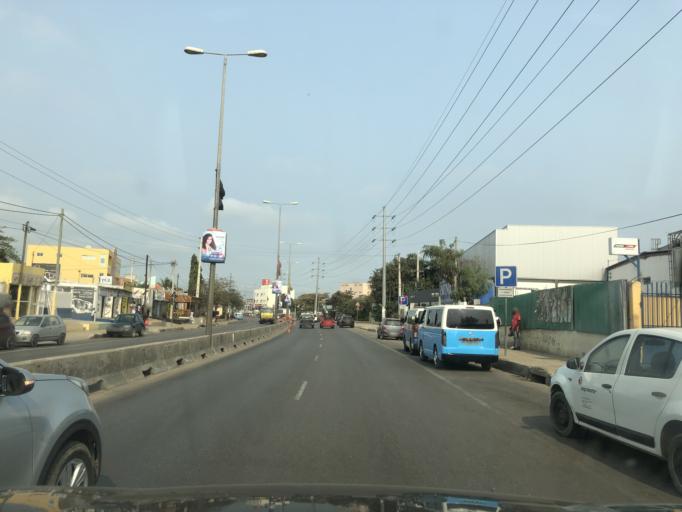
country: AO
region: Luanda
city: Luanda
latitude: -8.8933
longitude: 13.1852
